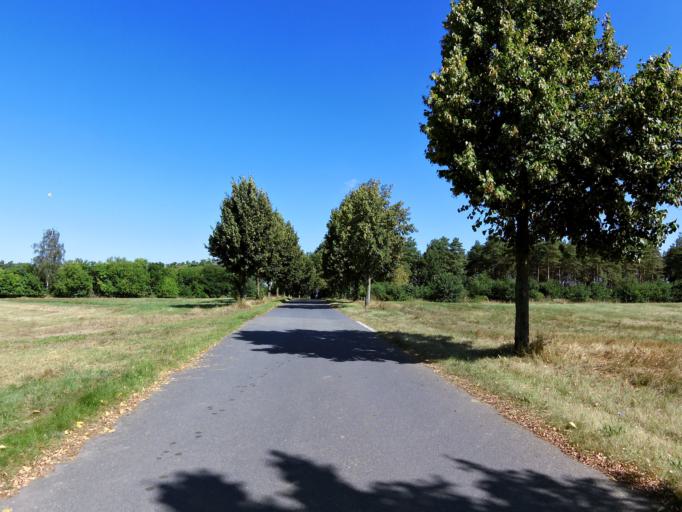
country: DE
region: Saxony
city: Strehla
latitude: 51.3823
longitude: 13.2616
